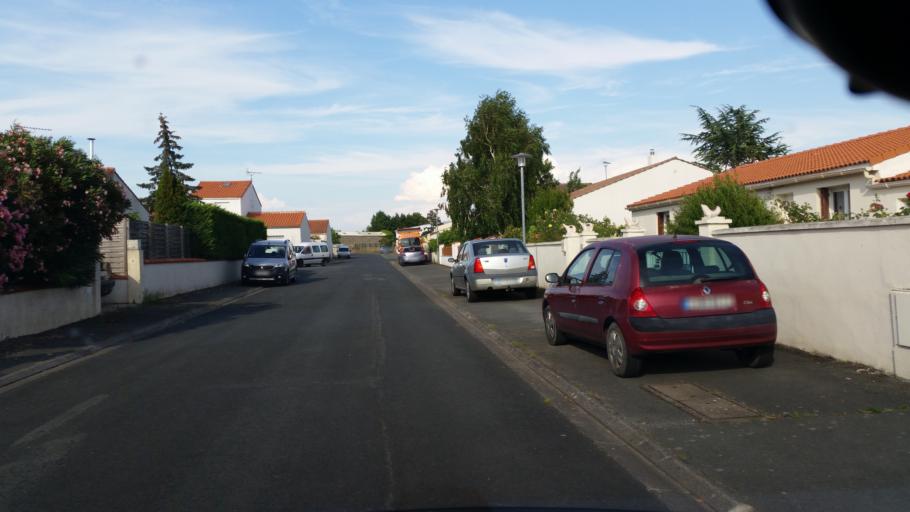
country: FR
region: Poitou-Charentes
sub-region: Departement de la Charente-Maritime
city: Marans
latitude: 46.3057
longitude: -1.0037
